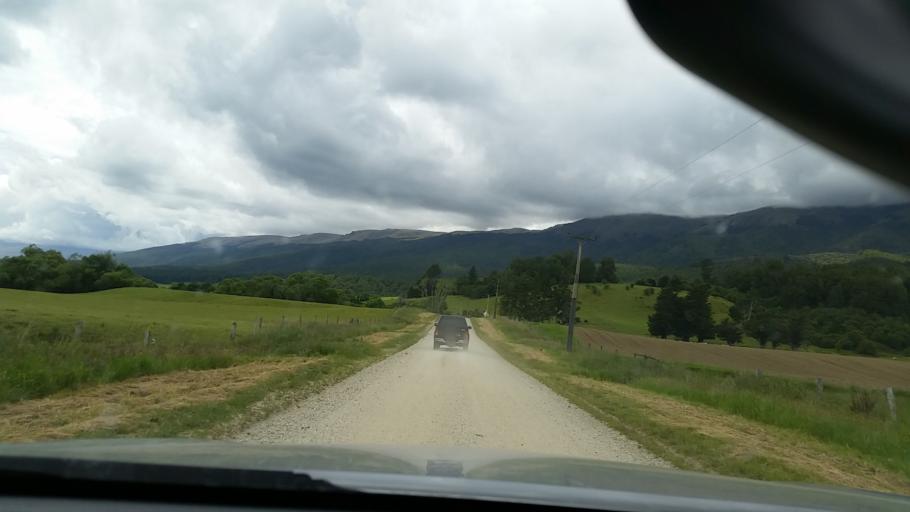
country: NZ
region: Otago
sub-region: Queenstown-Lakes District
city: Kingston
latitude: -45.5984
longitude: 168.9819
